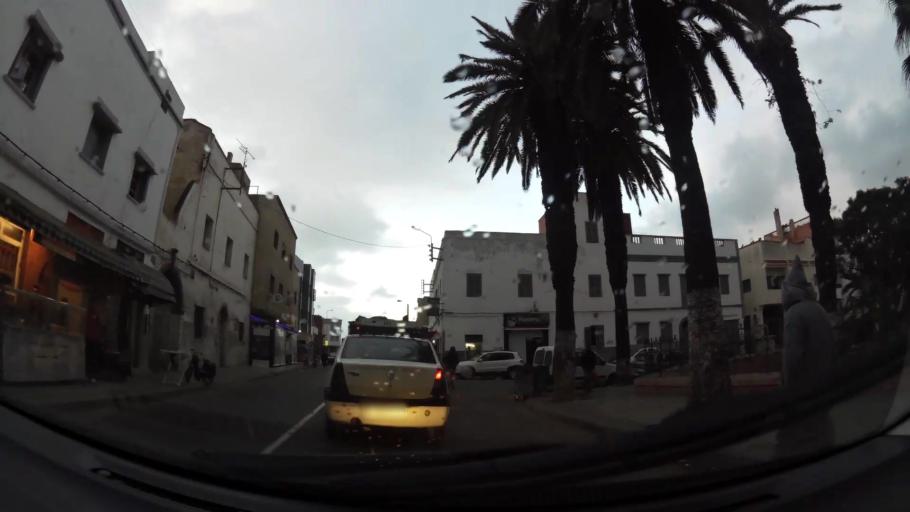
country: MA
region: Doukkala-Abda
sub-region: El-Jadida
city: El Jadida
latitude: 33.2584
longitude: -8.5058
